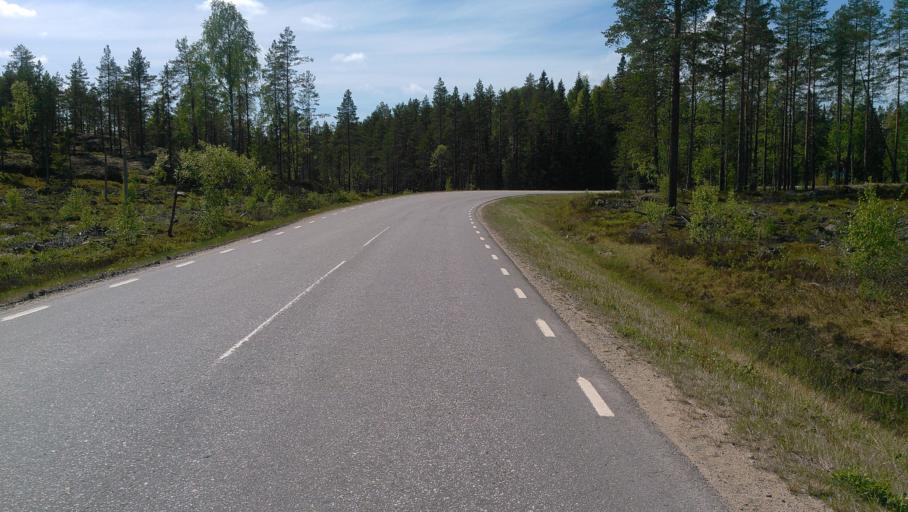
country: SE
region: Vaesterbotten
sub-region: Vannas Kommun
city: Vannasby
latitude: 63.8502
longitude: 19.9808
